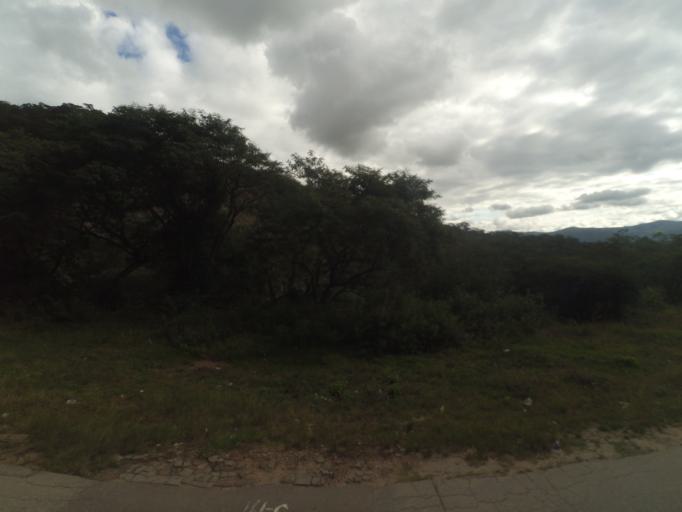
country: BO
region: Santa Cruz
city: Samaipata
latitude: -18.1666
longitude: -63.8962
